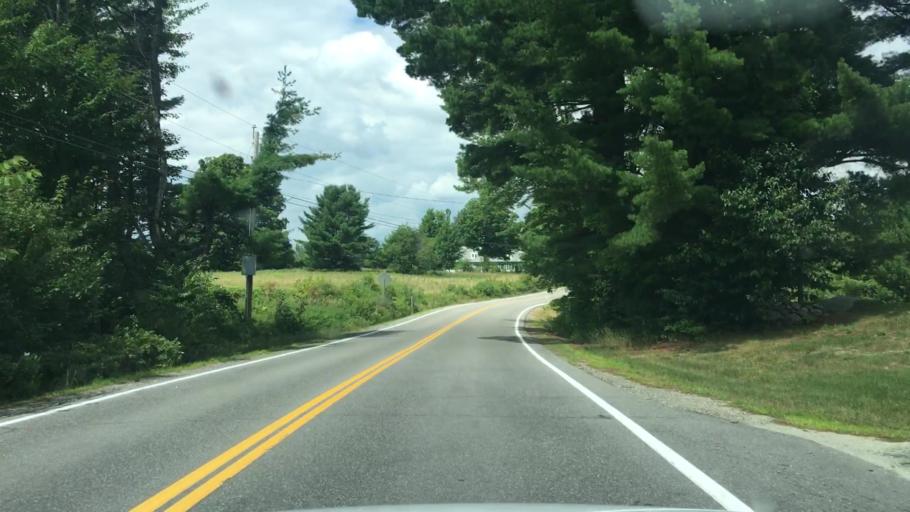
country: US
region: New Hampshire
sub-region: Coos County
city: Whitefield
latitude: 44.3079
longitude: -71.6590
